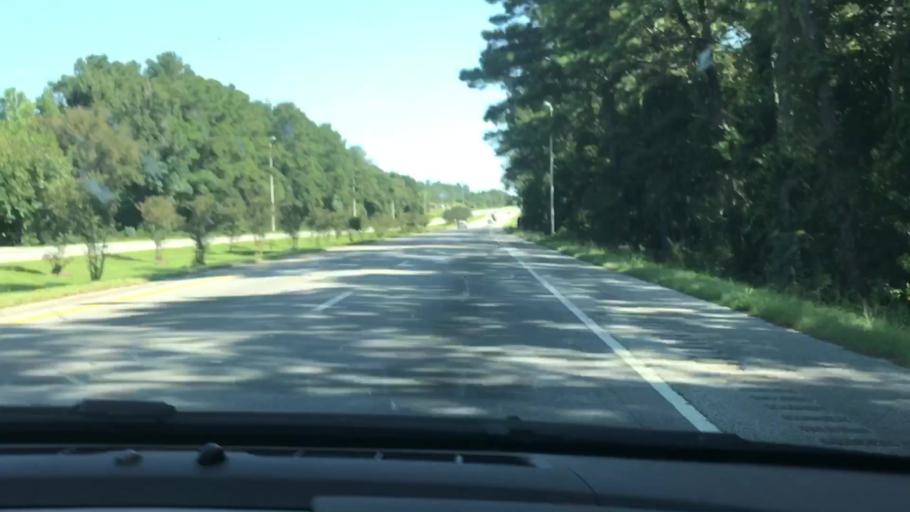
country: US
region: Alabama
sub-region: Russell County
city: Phenix City
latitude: 32.4435
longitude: -85.0198
